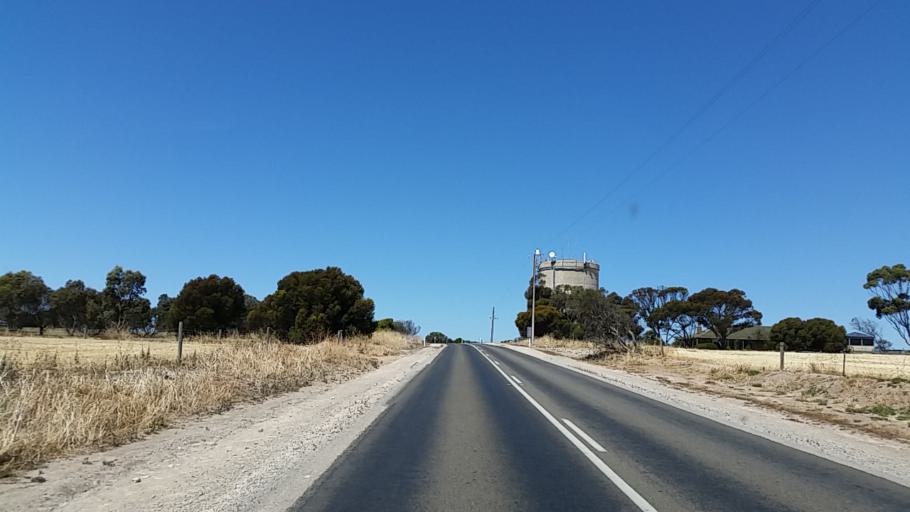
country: AU
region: South Australia
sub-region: Yorke Peninsula
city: Honiton
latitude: -35.0169
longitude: 137.6178
